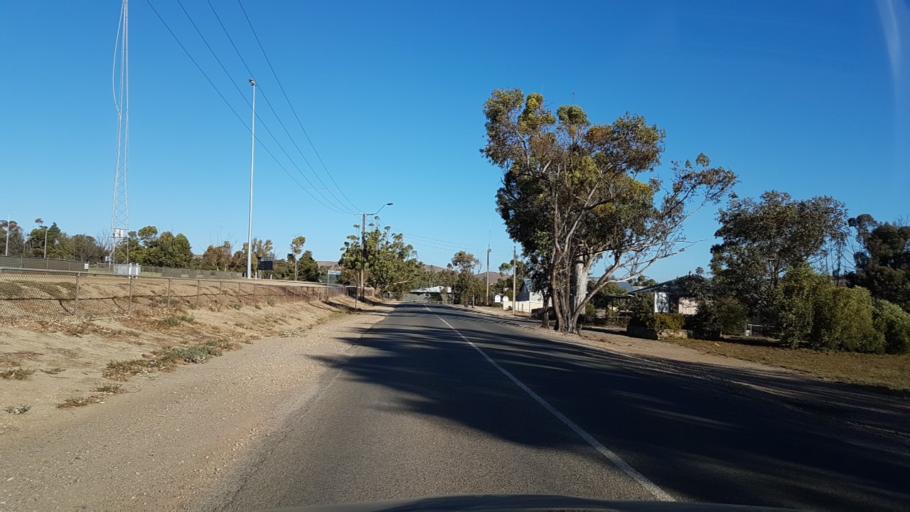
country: AU
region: South Australia
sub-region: Clare and Gilbert Valleys
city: Clare
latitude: -33.6764
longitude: 138.9401
